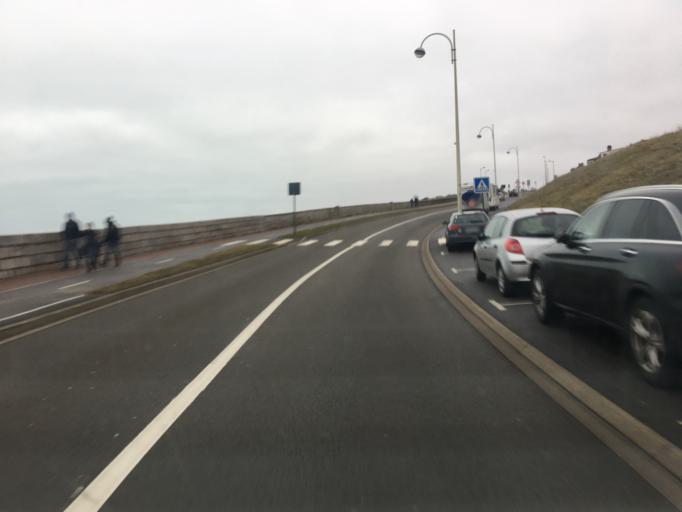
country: FR
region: Nord-Pas-de-Calais
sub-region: Departement du Pas-de-Calais
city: Saint-Martin-Boulogne
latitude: 50.7390
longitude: 1.5944
